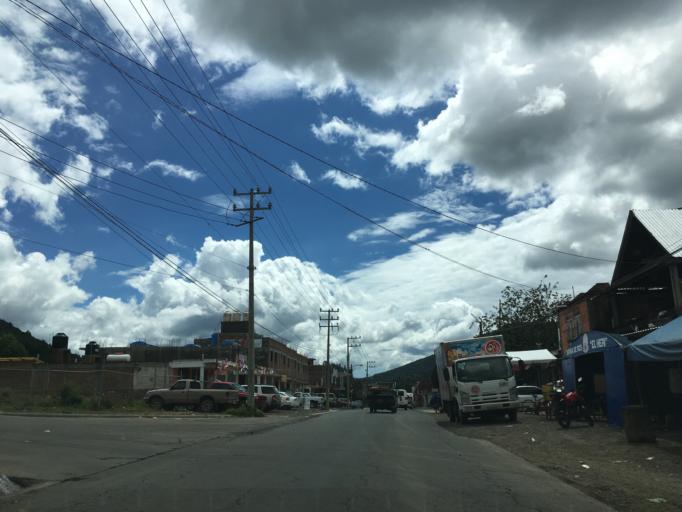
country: MX
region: Michoacan
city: Cheran
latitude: 19.6779
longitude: -101.9534
